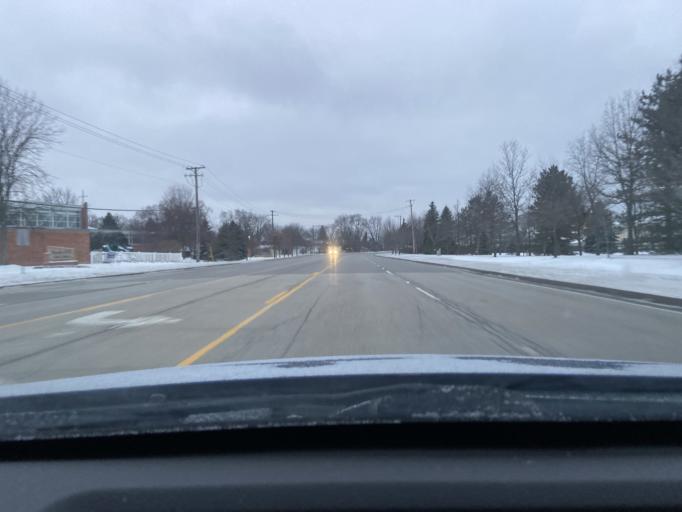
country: US
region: Illinois
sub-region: Lake County
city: Grayslake
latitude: 42.3583
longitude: -88.0386
